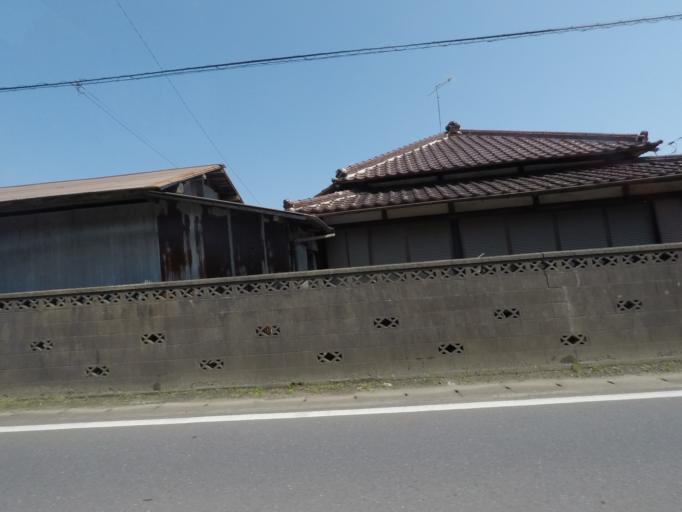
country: JP
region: Chiba
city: Yokaichiba
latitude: 35.6692
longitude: 140.4713
